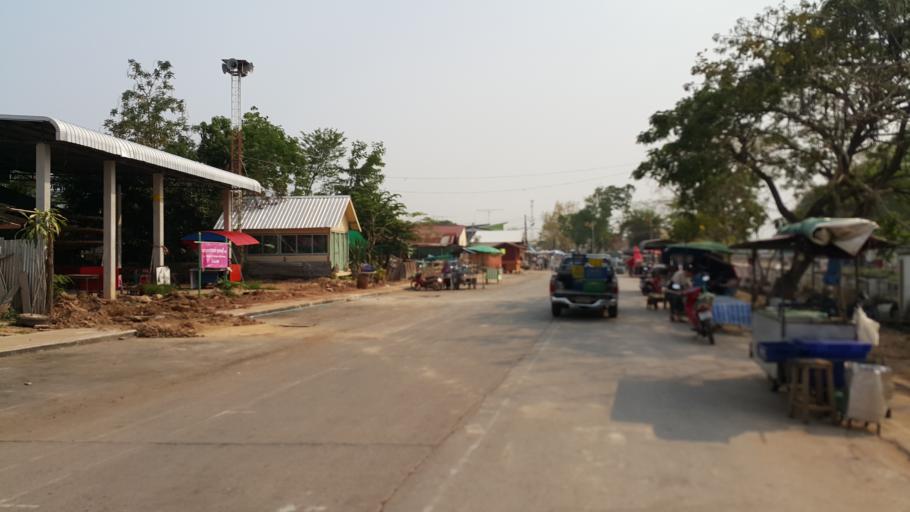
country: TH
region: Nakhon Phanom
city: That Phanom
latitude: 16.9452
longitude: 104.7274
